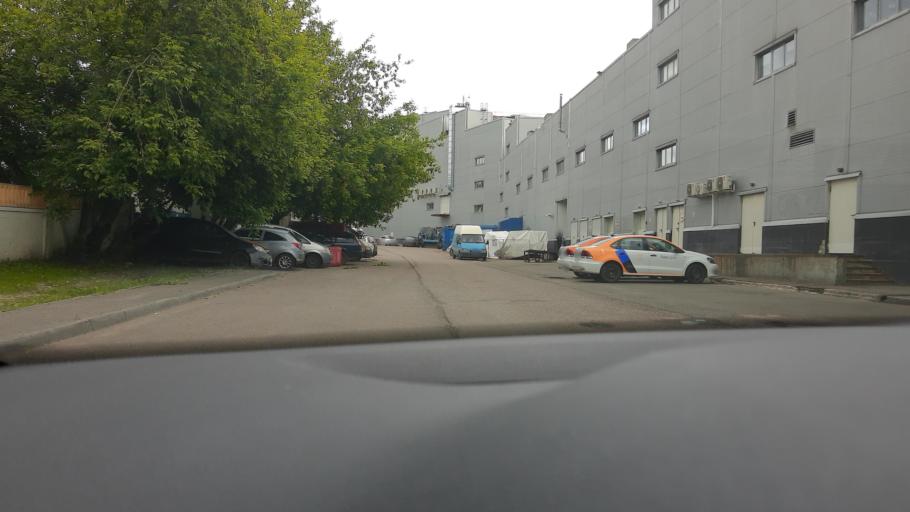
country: RU
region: Moscow
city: Rublevo
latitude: 55.7670
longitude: 37.3820
